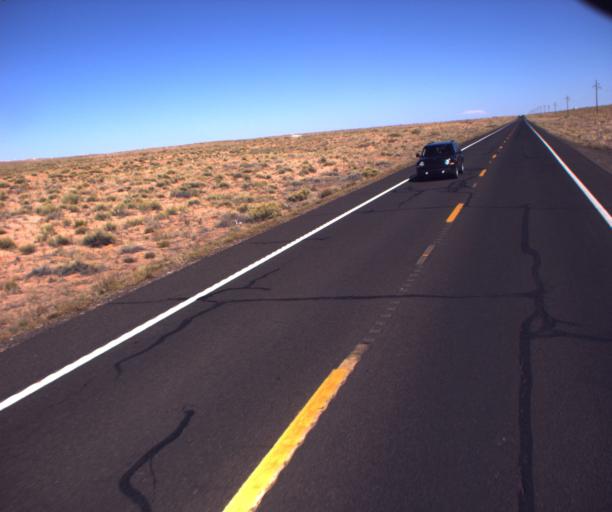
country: US
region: Arizona
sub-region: Coconino County
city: Tuba City
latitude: 36.1351
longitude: -111.1766
